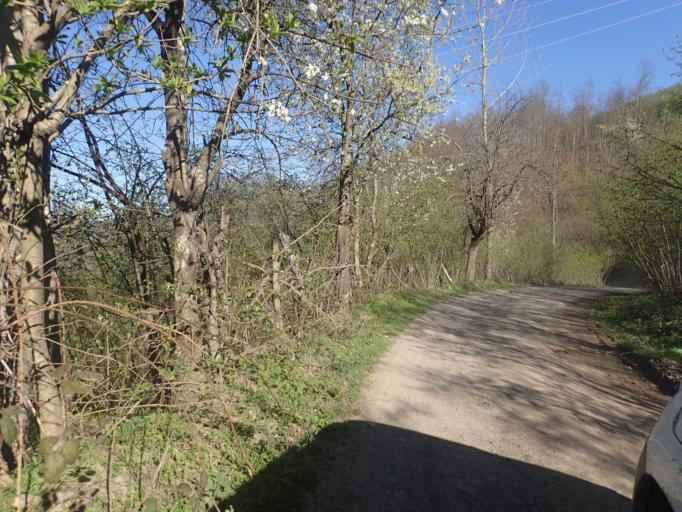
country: TR
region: Ordu
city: Korgan
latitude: 40.7605
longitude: 37.3095
